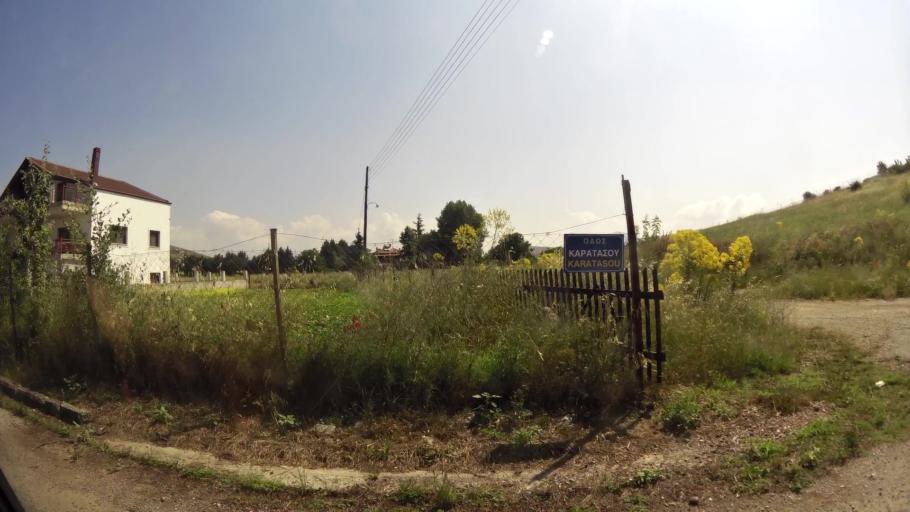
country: GR
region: West Macedonia
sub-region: Nomos Kozanis
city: Koila
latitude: 40.3398
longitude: 21.7887
